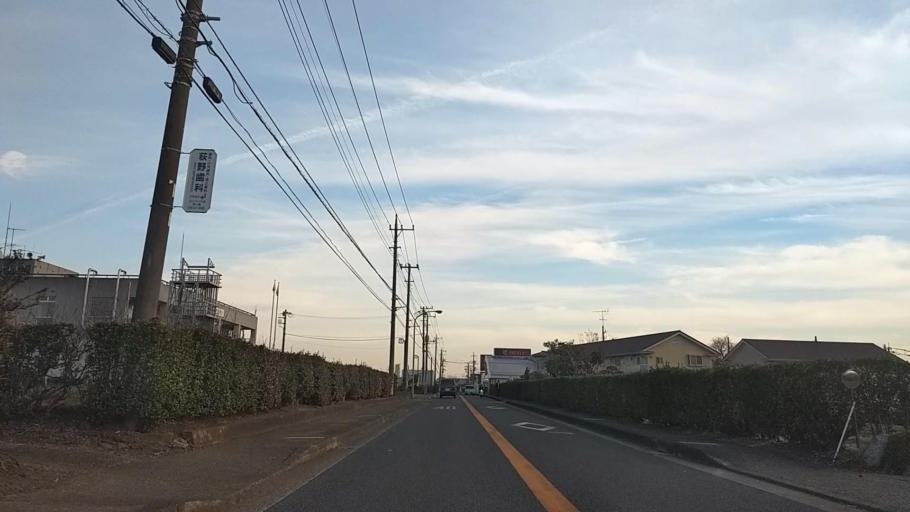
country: JP
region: Kanagawa
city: Atsugi
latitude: 35.4835
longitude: 139.3328
